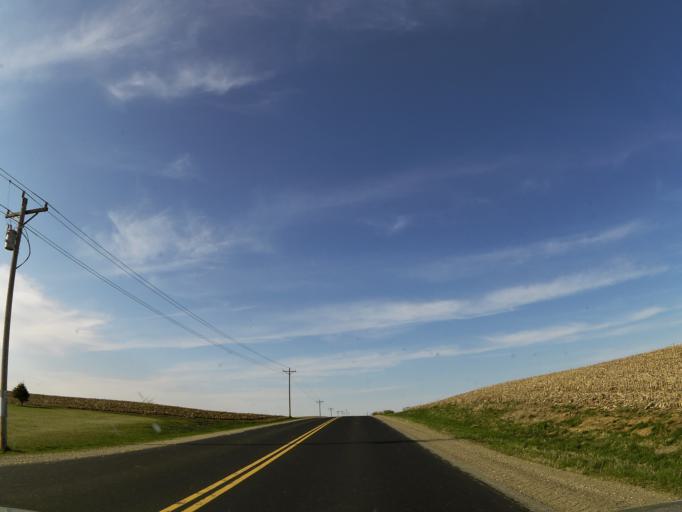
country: US
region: Wisconsin
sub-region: Pierce County
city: Ellsworth
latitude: 44.7214
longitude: -92.6090
